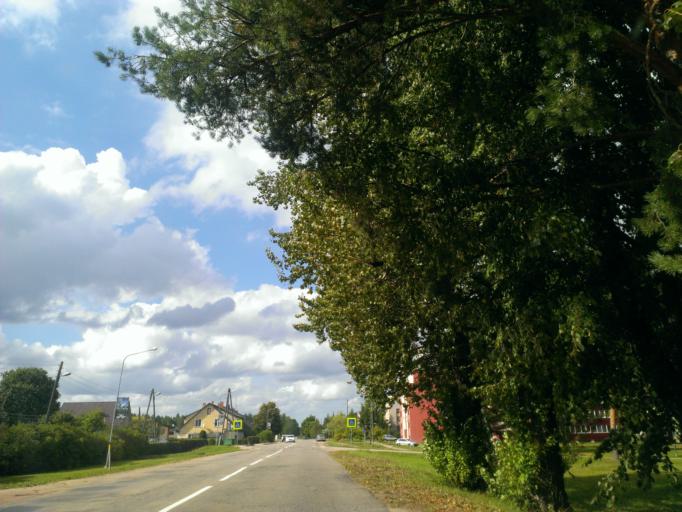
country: LV
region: Garkalne
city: Garkalne
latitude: 56.9688
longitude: 24.4839
